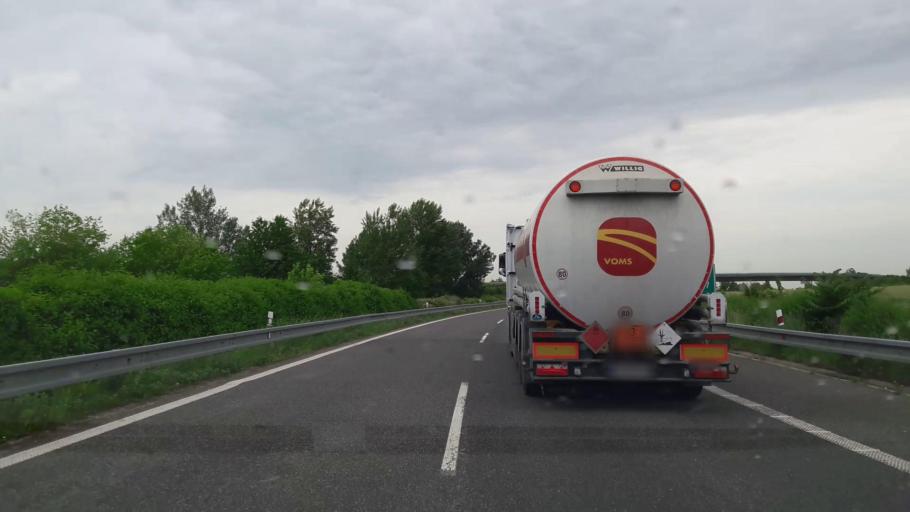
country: AT
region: Burgenland
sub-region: Politischer Bezirk Neusiedl am See
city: Kittsee
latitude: 48.0744
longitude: 17.1004
